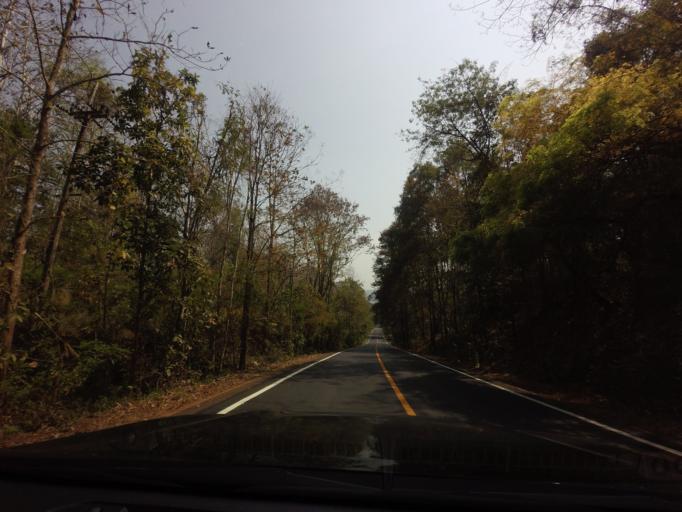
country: TH
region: Kanchanaburi
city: Thong Pha Phum
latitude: 14.7800
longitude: 98.5938
